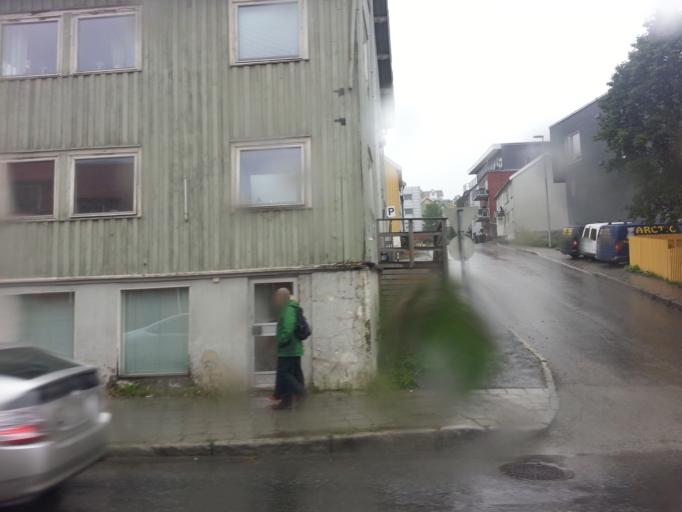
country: NO
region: Troms
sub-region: Tromso
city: Tromso
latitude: 69.6540
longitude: 18.9633
